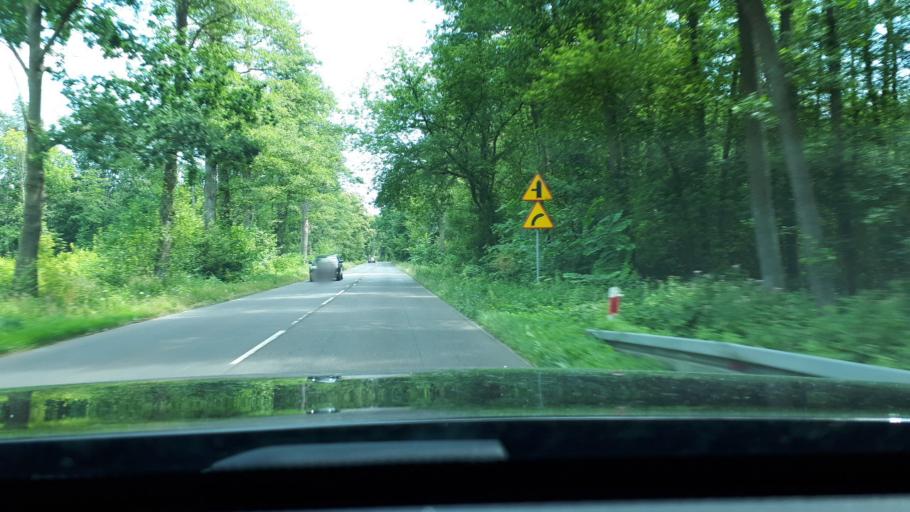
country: PL
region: Lodz Voivodeship
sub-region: powiat Lowicki
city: Nieborow
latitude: 52.0717
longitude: 20.0477
